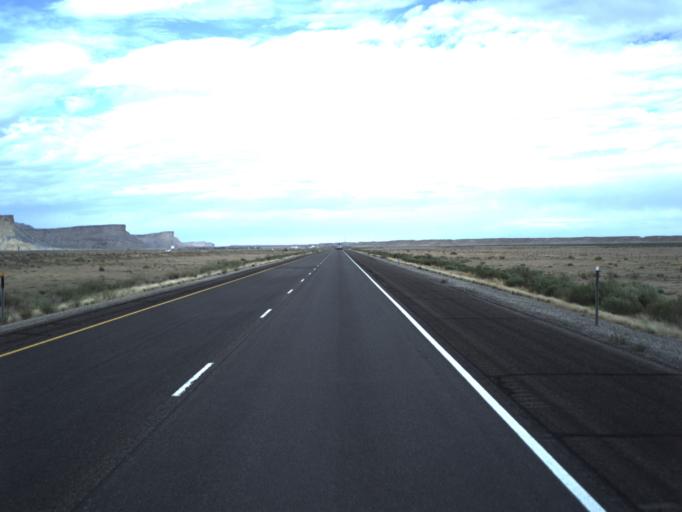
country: US
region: Utah
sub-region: Grand County
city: Moab
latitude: 38.9476
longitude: -109.7860
